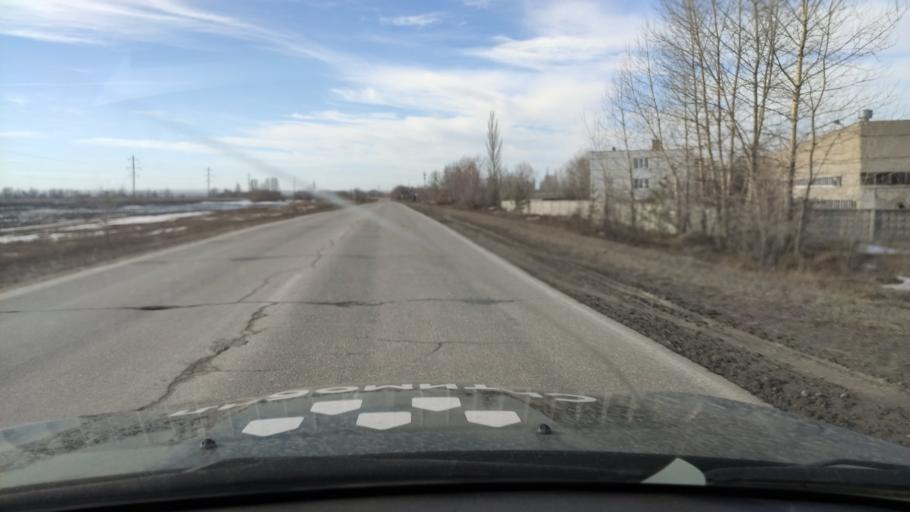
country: RU
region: Samara
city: Povolzhskiy
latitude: 53.5788
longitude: 49.6972
